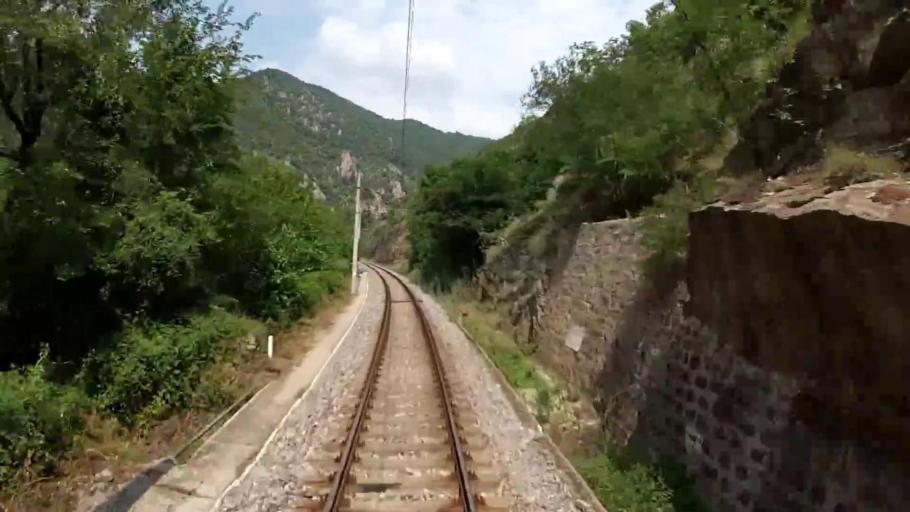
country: BG
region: Blagoevgrad
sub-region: Obshtina Kresna
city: Stara Kresna
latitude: 41.8004
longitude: 23.1607
